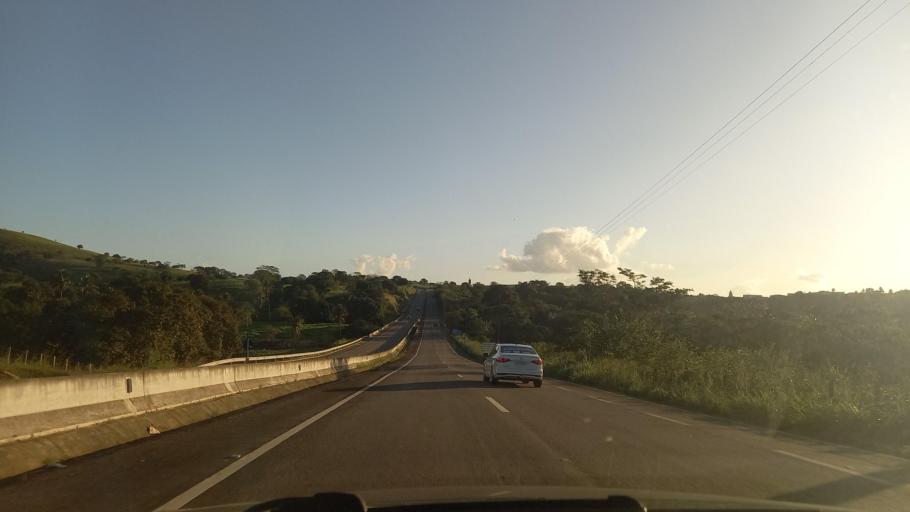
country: BR
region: Alagoas
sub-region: Limoeiro De Anadia
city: Limoeiro de Anadia
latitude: -9.7391
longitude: -36.4929
